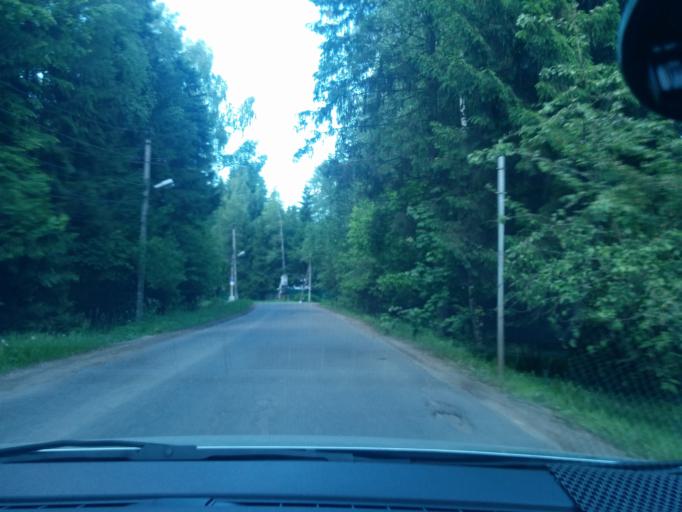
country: RU
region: Moskovskaya
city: Lugovaya
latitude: 56.0516
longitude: 37.5135
